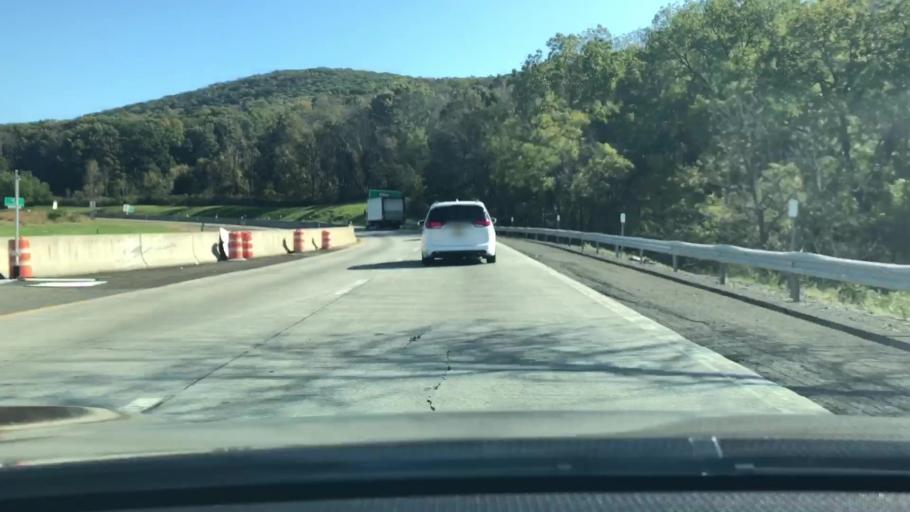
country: US
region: New York
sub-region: Orange County
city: Harriman
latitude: 41.3078
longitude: -74.1247
